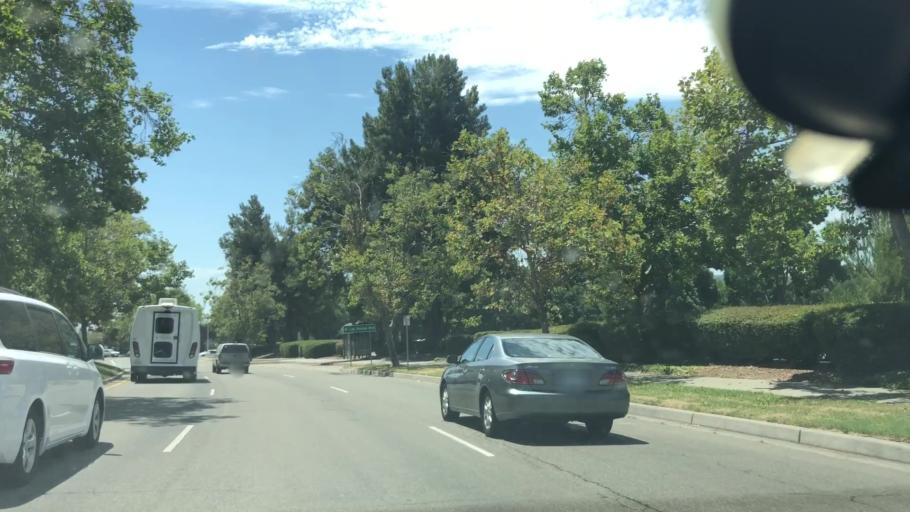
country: US
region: California
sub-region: Alameda County
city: Pleasanton
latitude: 37.6938
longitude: -121.8787
